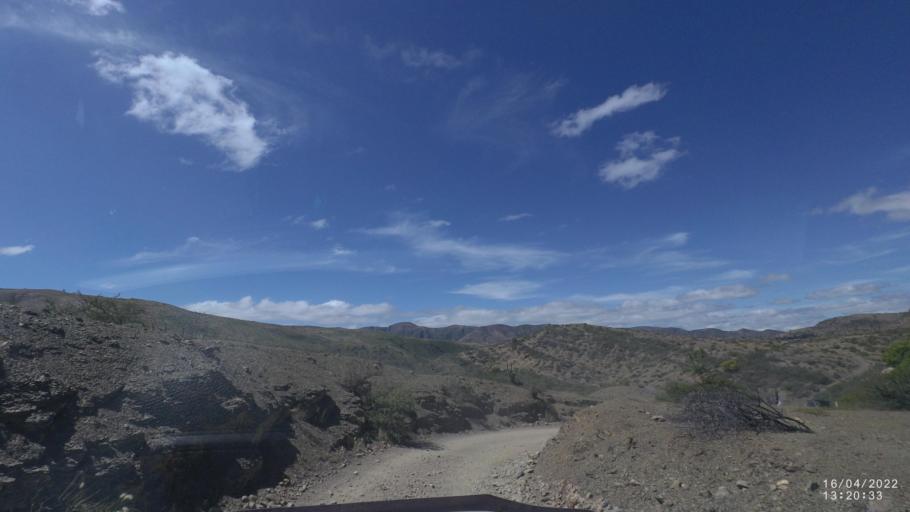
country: BO
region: Cochabamba
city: Mizque
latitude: -17.9900
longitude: -65.6122
